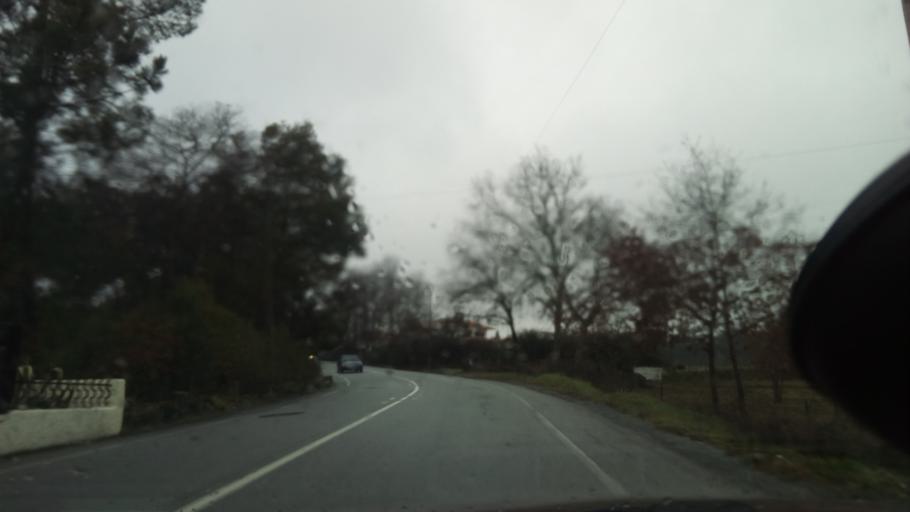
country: PT
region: Viseu
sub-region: Viseu
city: Rio de Loba
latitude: 40.6578
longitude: -7.8734
